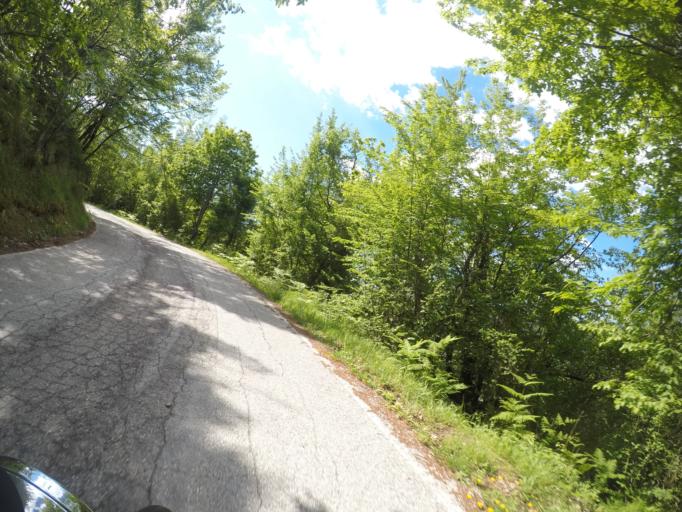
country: IT
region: Tuscany
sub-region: Provincia di Lucca
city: Minucciano
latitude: 44.1666
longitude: 10.2073
